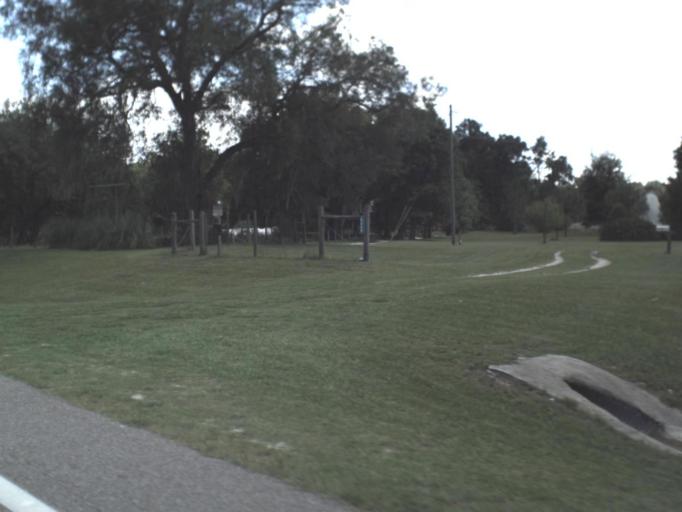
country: US
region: Florida
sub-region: Lafayette County
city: Mayo
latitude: 30.0359
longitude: -83.0667
